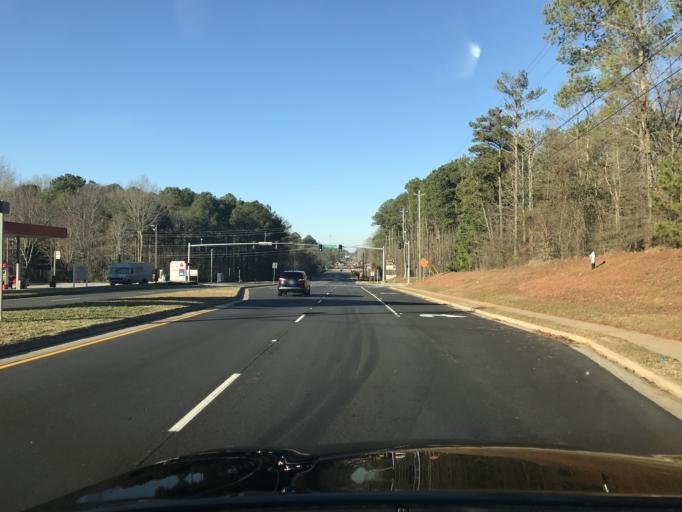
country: US
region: Georgia
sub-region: Clayton County
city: Jonesboro
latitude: 33.5181
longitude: -84.3742
